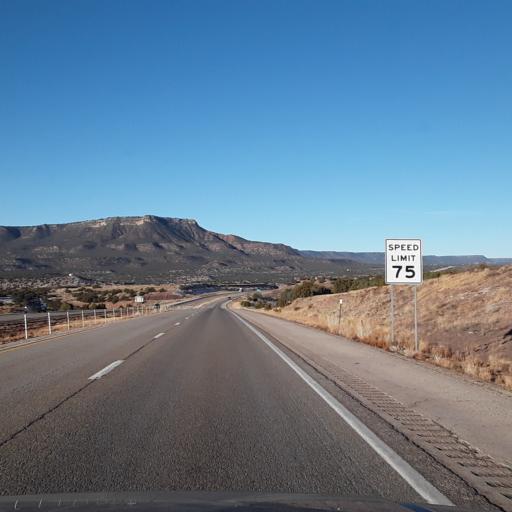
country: US
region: New Mexico
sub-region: San Miguel County
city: Pecos
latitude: 35.3969
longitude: -105.4554
